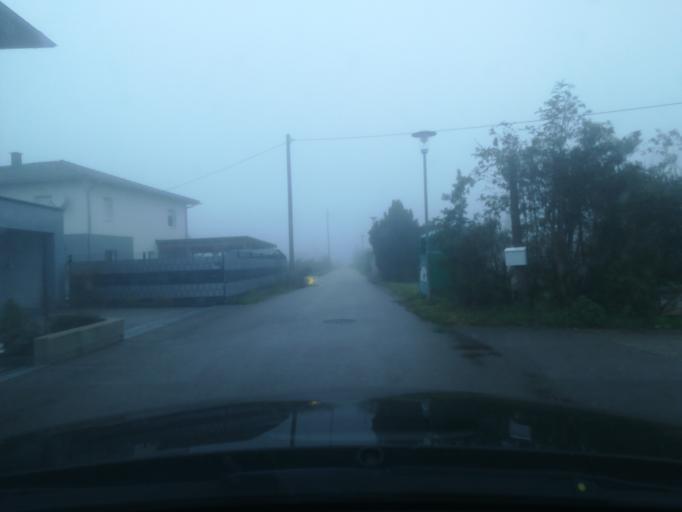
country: AT
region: Upper Austria
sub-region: Wels-Land
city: Marchtrenk
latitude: 48.1990
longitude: 14.1409
